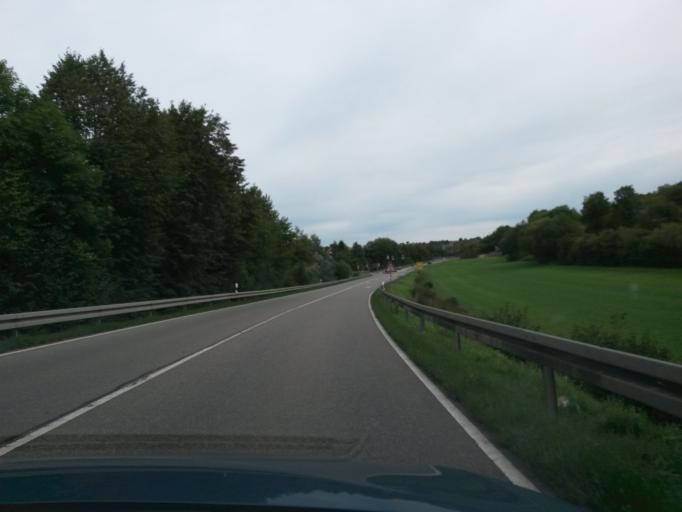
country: DE
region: Baden-Wuerttemberg
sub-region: Karlsruhe Region
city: Konigsbach-Stein
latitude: 48.9623
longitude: 8.5980
